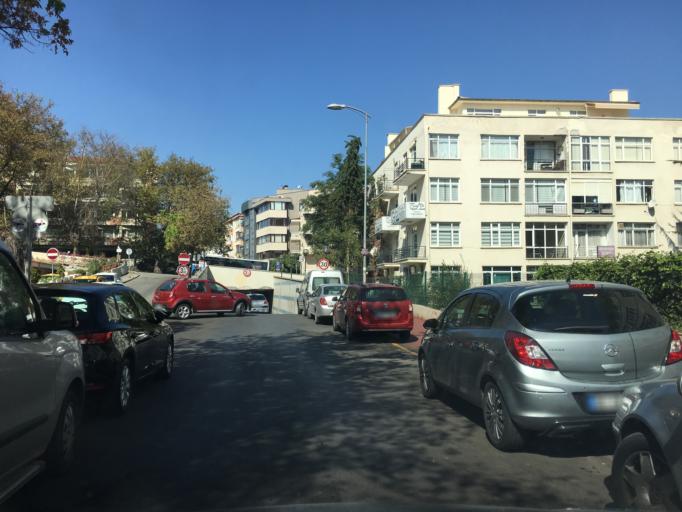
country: TR
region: Ankara
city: Cankaya
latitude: 39.8964
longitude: 32.8588
